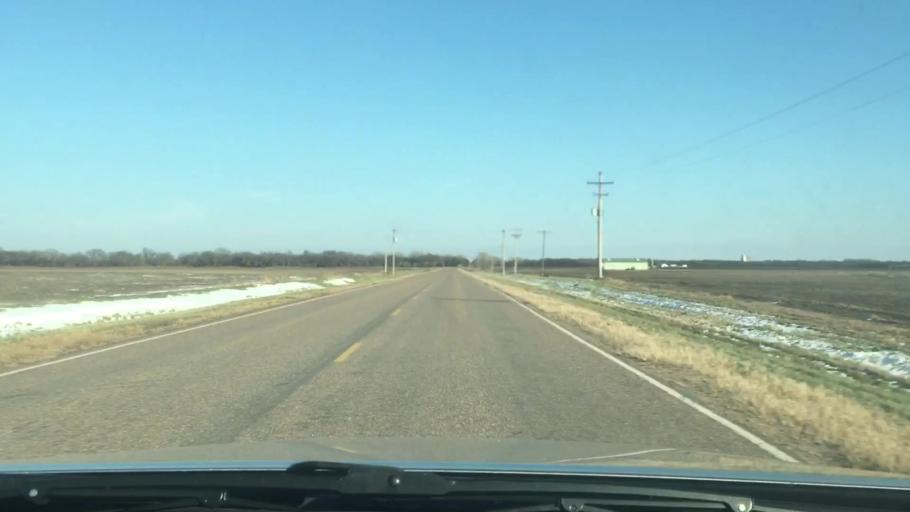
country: US
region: Kansas
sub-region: Rice County
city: Lyons
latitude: 38.2895
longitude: -98.1612
